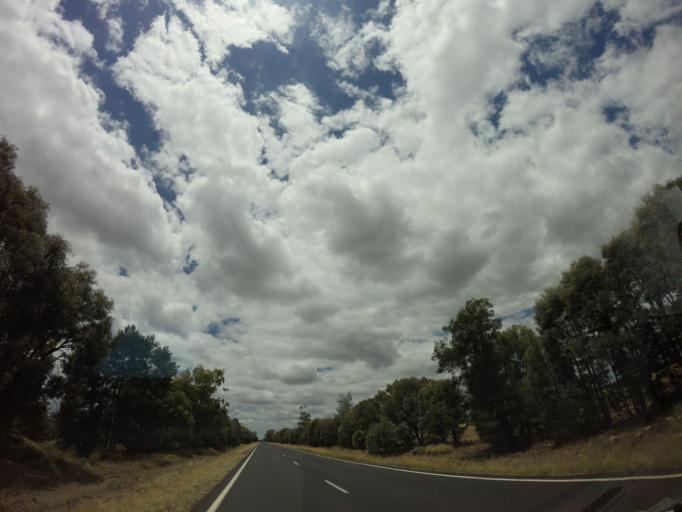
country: AU
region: Queensland
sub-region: Goondiwindi
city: Goondiwindi
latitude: -28.1708
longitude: 150.5063
